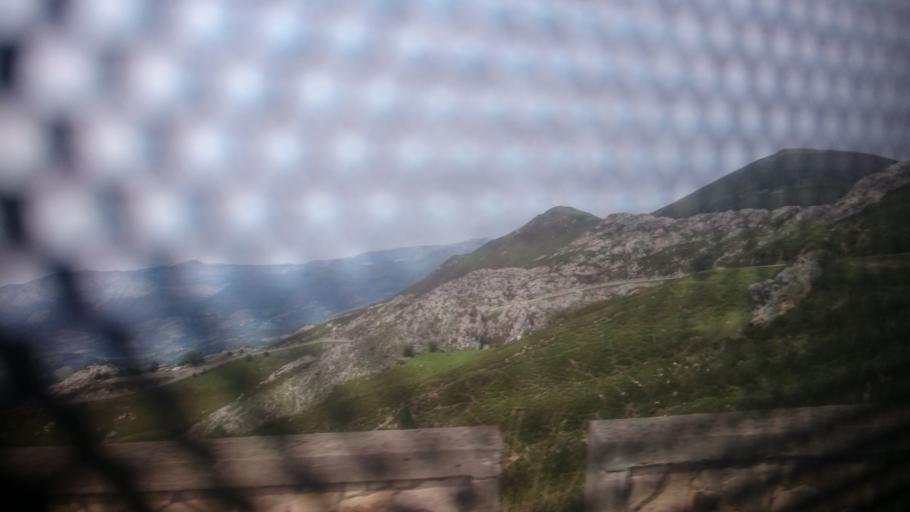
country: ES
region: Asturias
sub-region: Province of Asturias
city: Amieva
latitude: 43.2866
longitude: -5.0077
